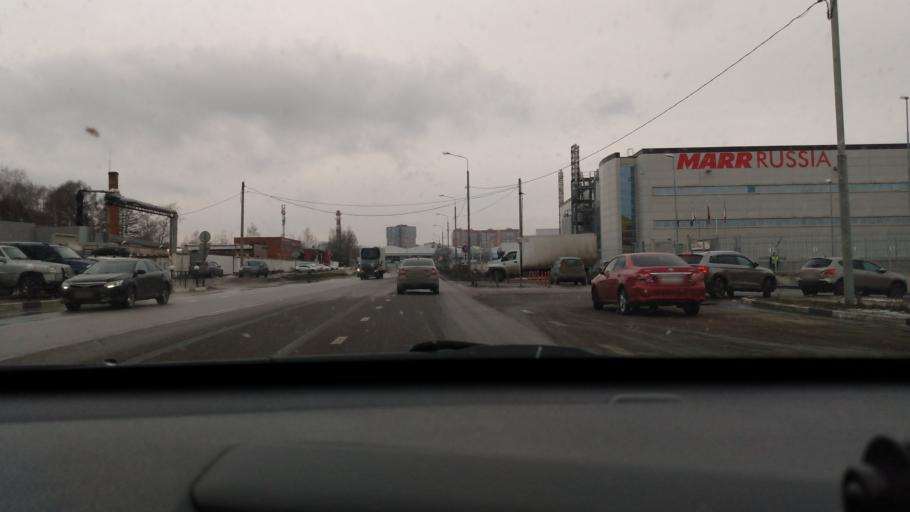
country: RU
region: Moskovskaya
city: Odintsovo
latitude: 55.6713
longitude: 37.3046
